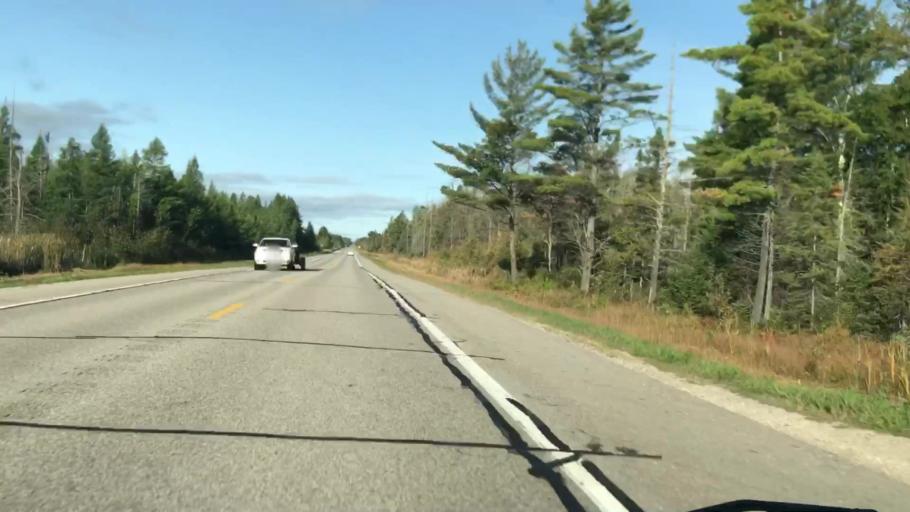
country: US
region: Michigan
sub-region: Luce County
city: Newberry
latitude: 46.3036
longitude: -85.3127
